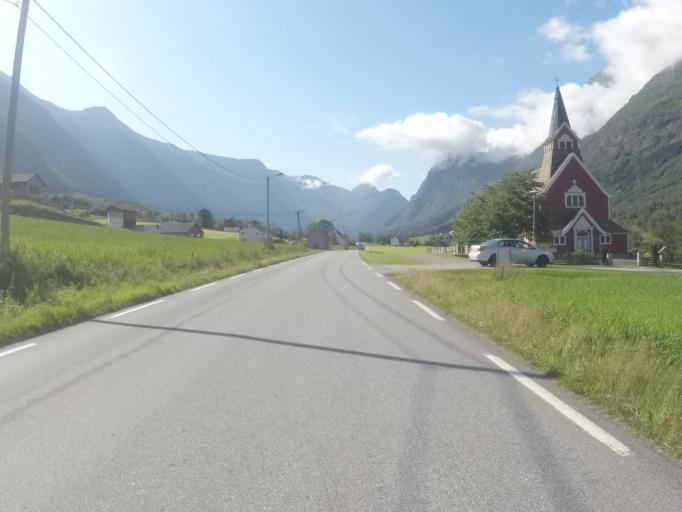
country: NO
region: Sogn og Fjordane
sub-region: Stryn
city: Stryn
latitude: 61.8283
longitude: 6.8085
